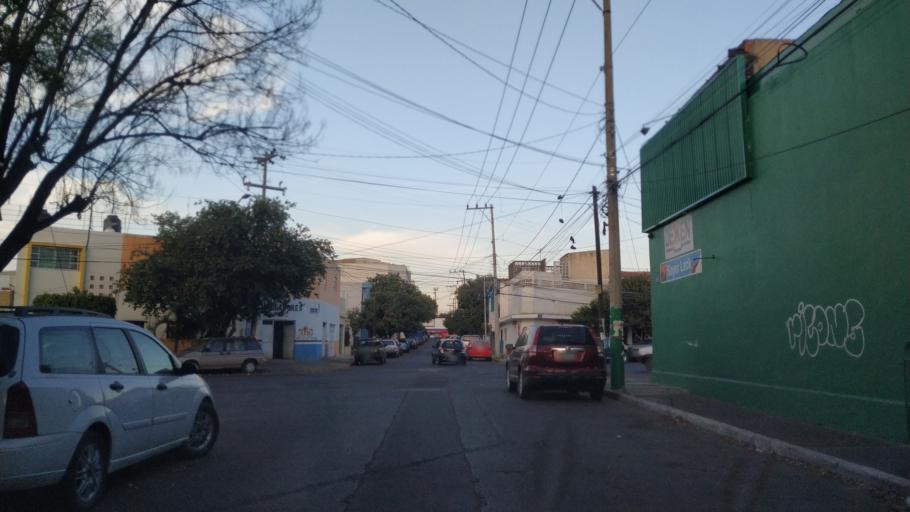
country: MX
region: Jalisco
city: Tlaquepaque
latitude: 20.6514
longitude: -103.3275
